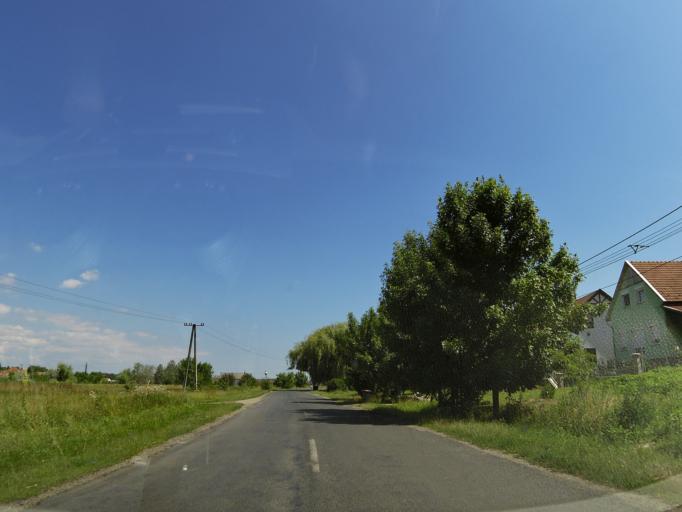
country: HU
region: Jasz-Nagykun-Szolnok
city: Abadszalok
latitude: 47.4678
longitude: 20.5933
